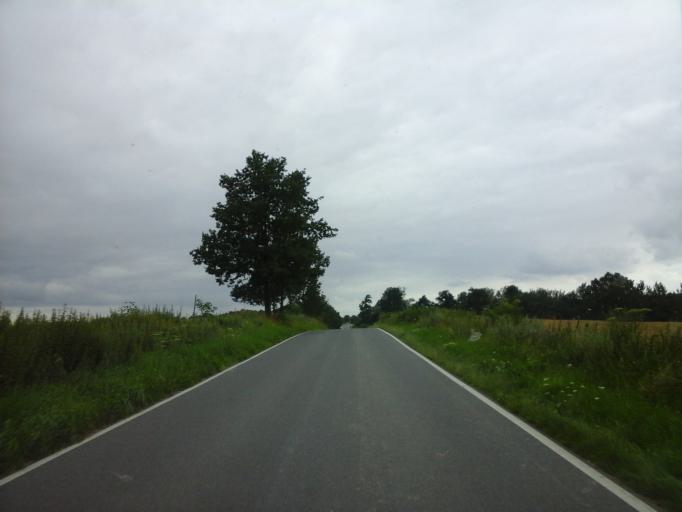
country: PL
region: West Pomeranian Voivodeship
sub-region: Powiat choszczenski
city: Pelczyce
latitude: 53.0080
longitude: 15.3935
